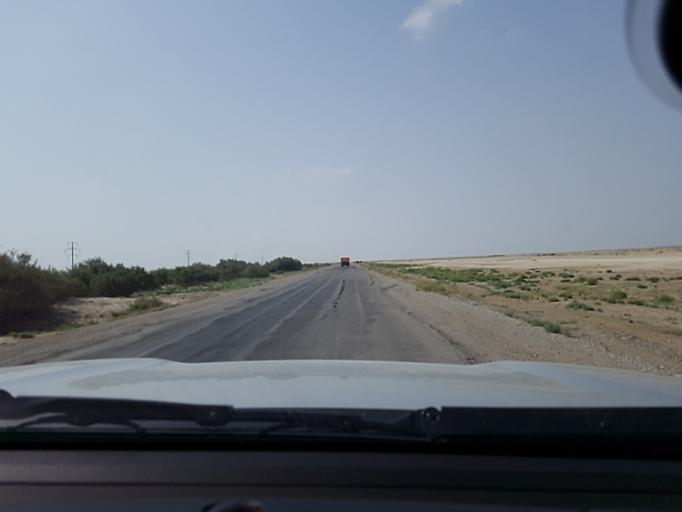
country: TM
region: Balkan
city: Gumdag
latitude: 38.9222
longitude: 54.5910
